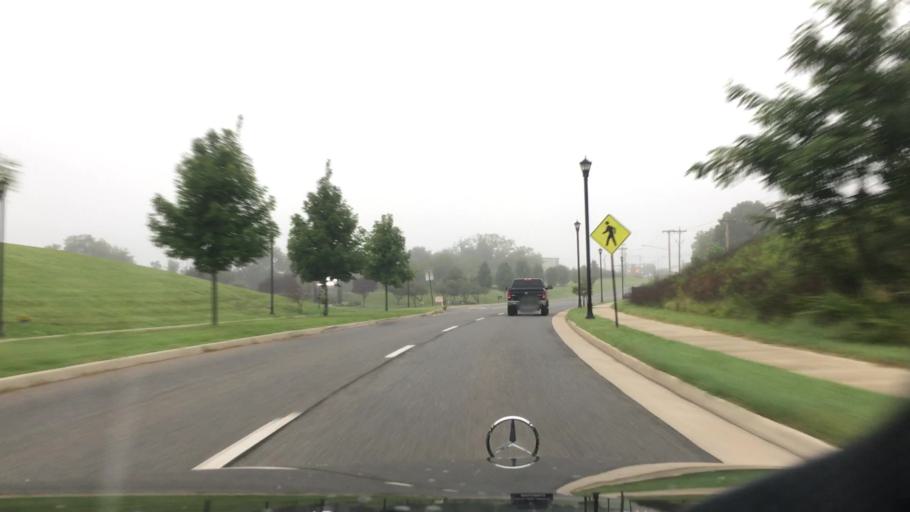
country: US
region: Virginia
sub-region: Campbell County
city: Timberlake
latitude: 37.3419
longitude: -79.2310
